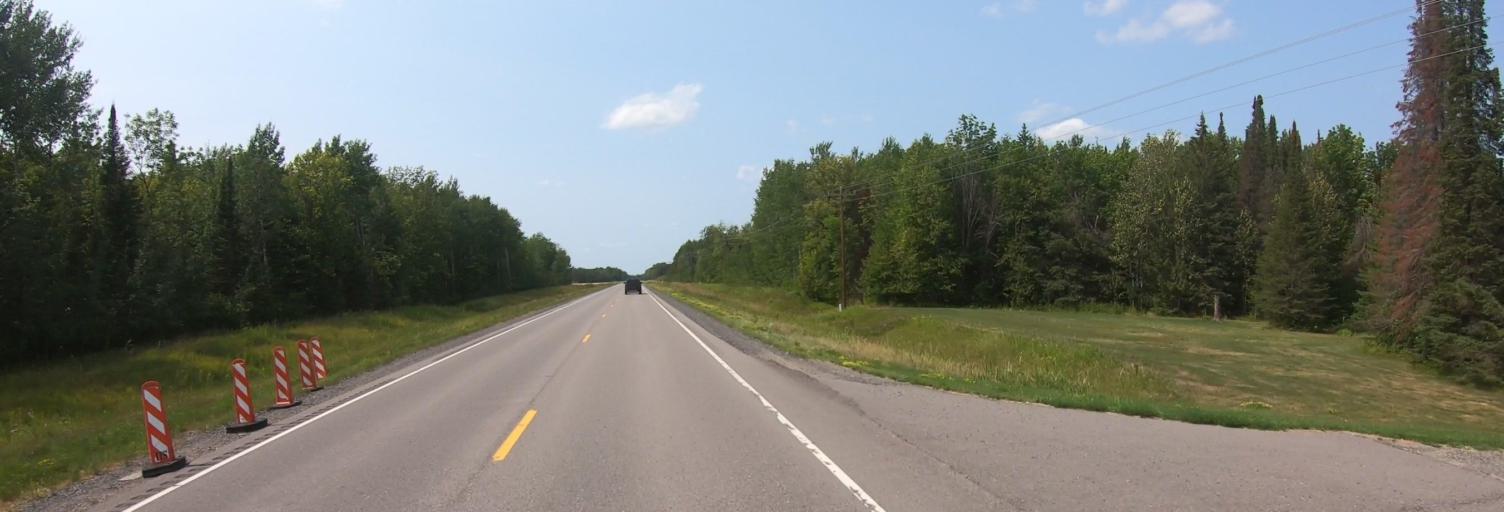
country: US
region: Minnesota
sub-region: Lake of the Woods County
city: Baudette
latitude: 48.6960
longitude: -94.5131
